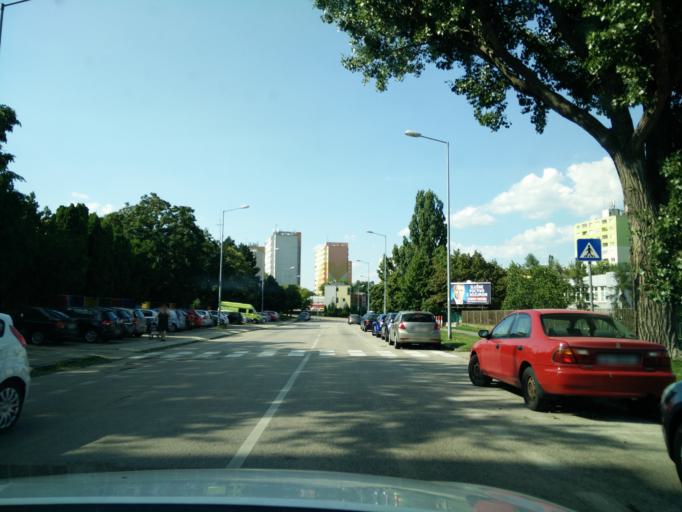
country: AT
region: Lower Austria
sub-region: Politischer Bezirk Bruck an der Leitha
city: Wolfsthal
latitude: 48.1923
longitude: 17.0285
